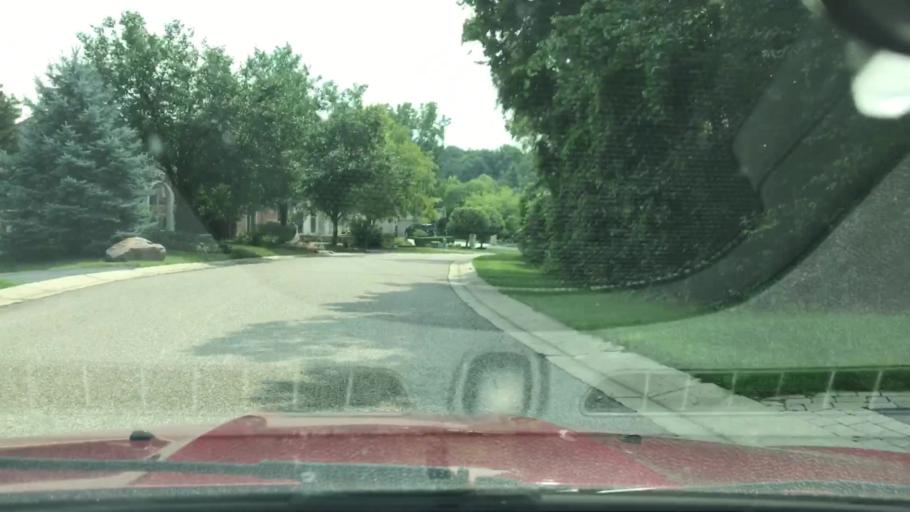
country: US
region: Michigan
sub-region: Oakland County
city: Wolverine Lake
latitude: 42.5372
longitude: -83.4321
